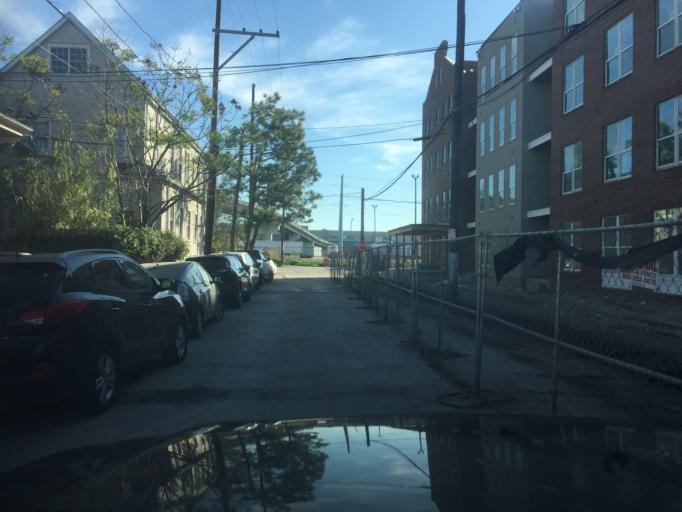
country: US
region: Louisiana
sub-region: Orleans Parish
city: New Orleans
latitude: 29.9378
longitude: -90.0695
